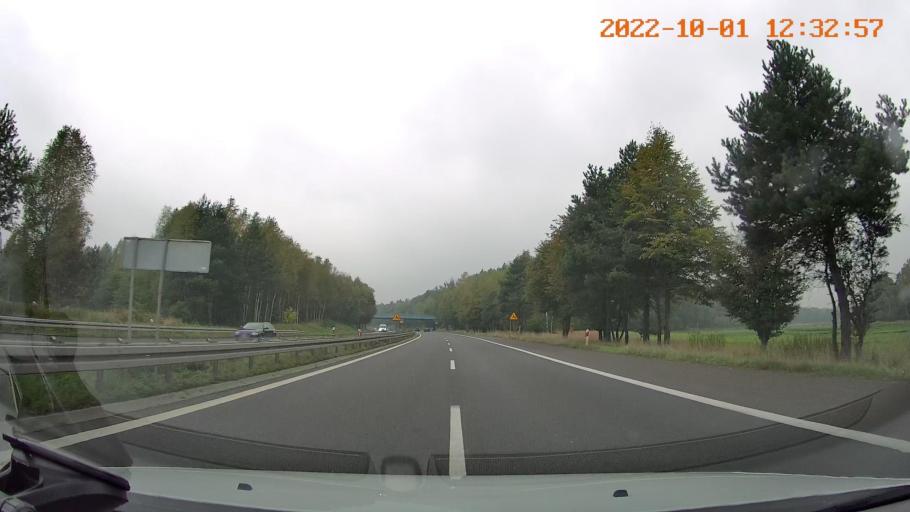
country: PL
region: Silesian Voivodeship
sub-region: Powiat bierunsko-ledzinski
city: Ledziny
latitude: 50.1548
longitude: 19.1250
